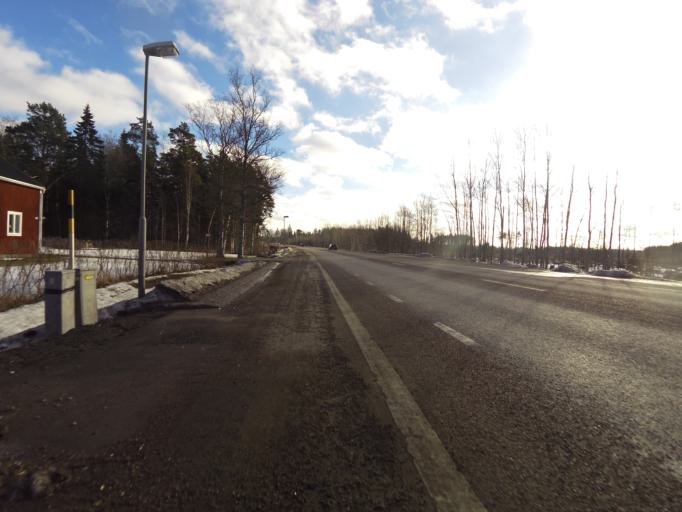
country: SE
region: Gaevleborg
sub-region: Gavle Kommun
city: Gavle
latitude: 60.6463
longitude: 17.2577
